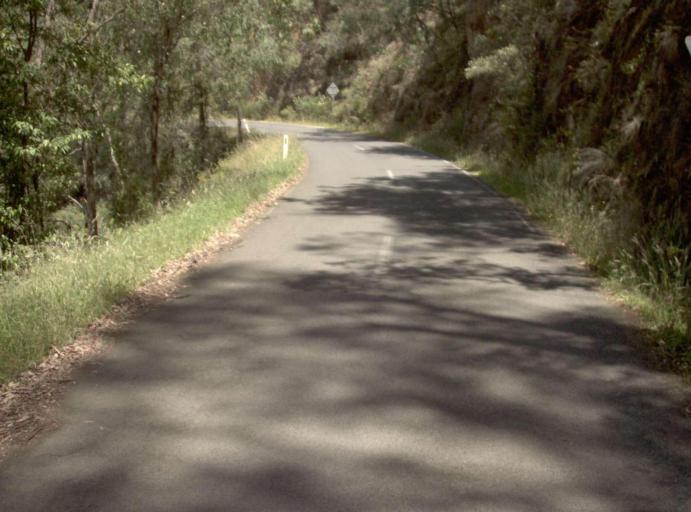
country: AU
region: Victoria
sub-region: Latrobe
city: Traralgon
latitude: -37.9522
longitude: 146.4399
